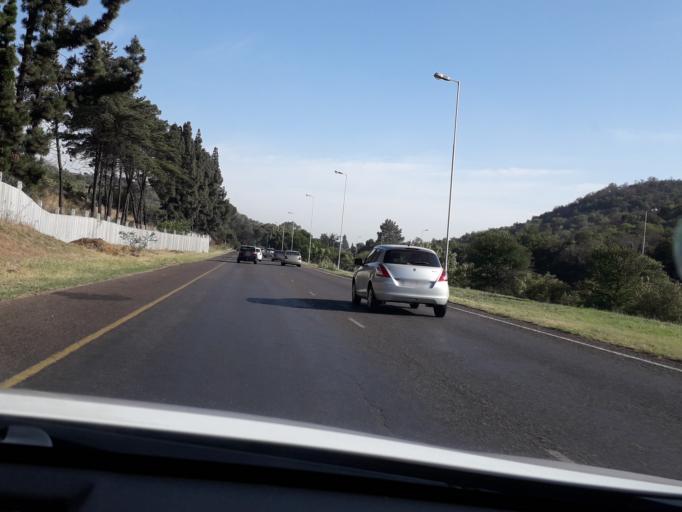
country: ZA
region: Gauteng
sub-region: City of Tshwane Metropolitan Municipality
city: Pretoria
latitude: -25.8006
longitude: 28.1970
